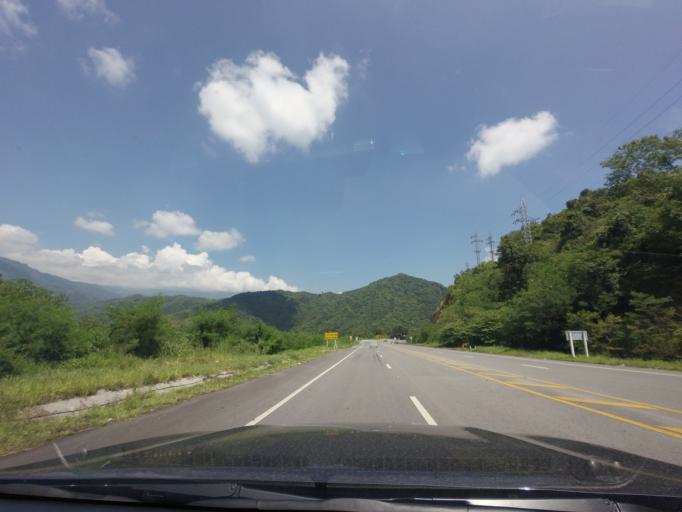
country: TH
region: Phetchabun
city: Khao Kho
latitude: 16.7810
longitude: 101.0942
